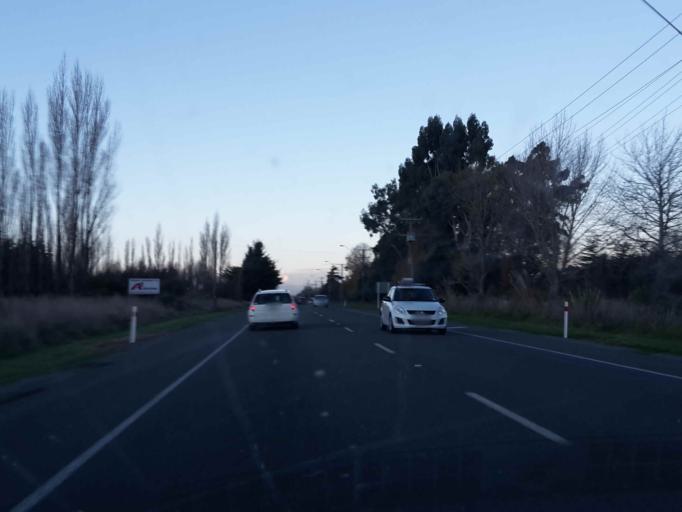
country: NZ
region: Canterbury
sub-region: Selwyn District
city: Prebbleton
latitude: -43.5521
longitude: 172.4810
